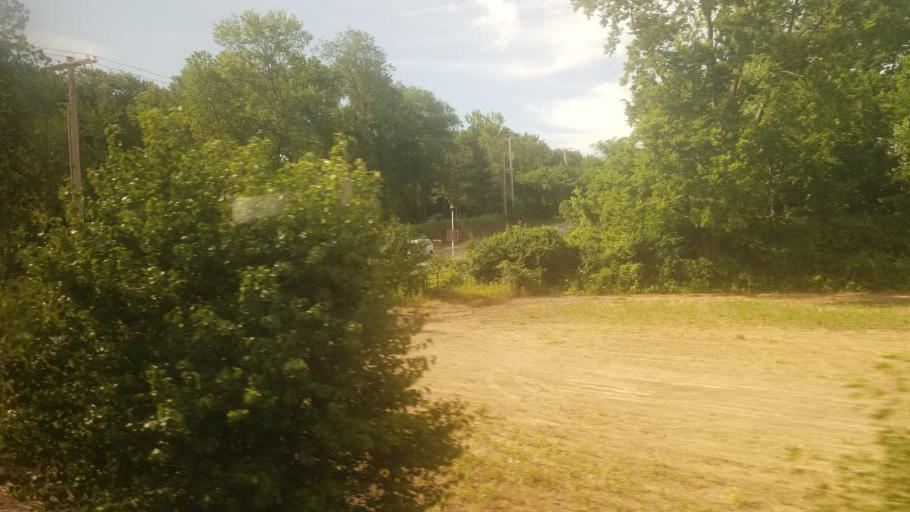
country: US
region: Kansas
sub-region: Wyandotte County
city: Edwardsville
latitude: 39.0479
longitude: -94.8305
